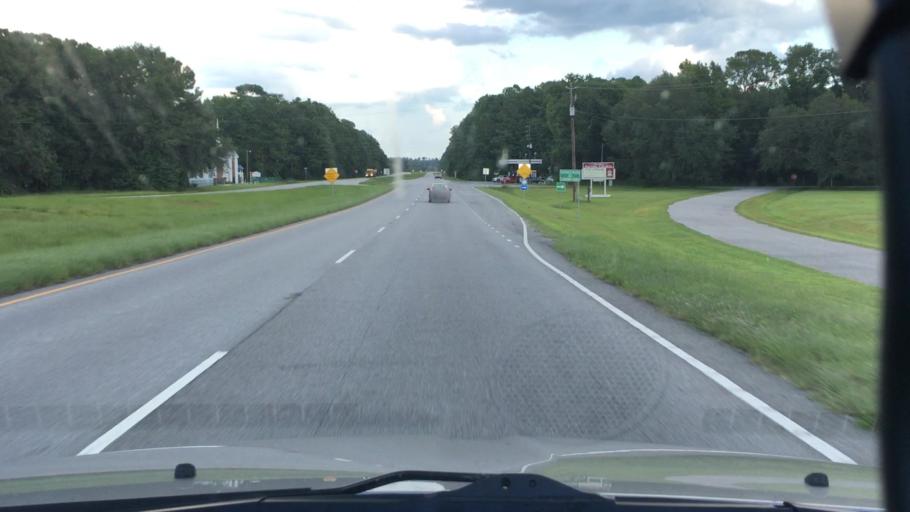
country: US
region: South Carolina
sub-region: Hampton County
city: Yemassee
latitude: 32.6015
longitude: -80.7950
